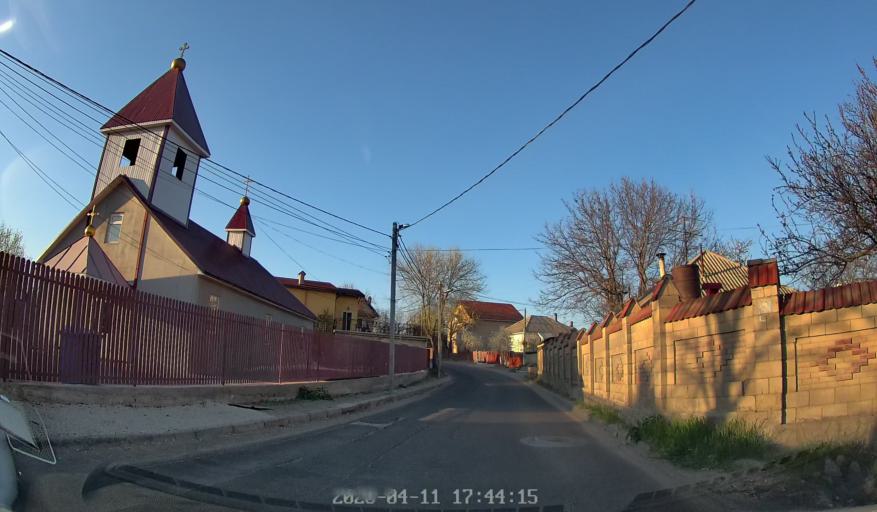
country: MD
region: Chisinau
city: Chisinau
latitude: 46.9770
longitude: 28.8238
